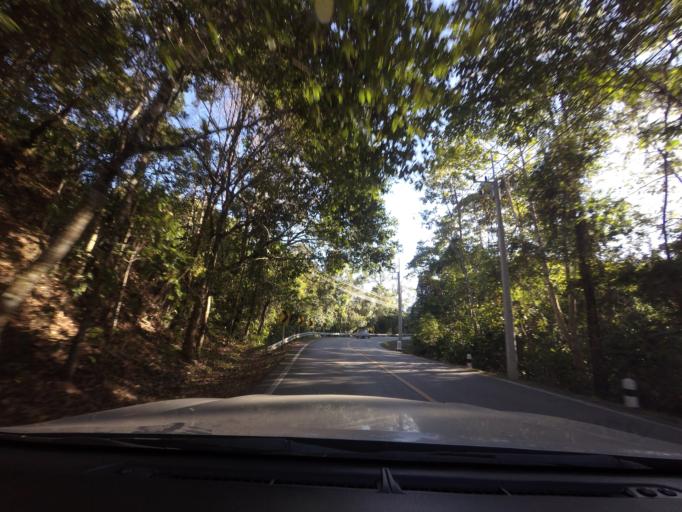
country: TH
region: Mae Hong Son
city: Mae Hi
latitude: 19.2724
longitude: 98.5991
